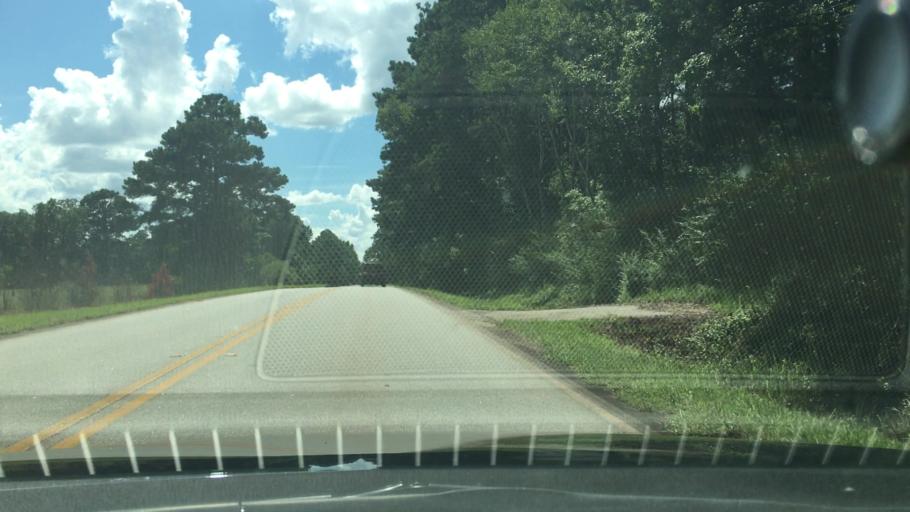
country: US
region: Georgia
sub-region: Jasper County
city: Monticello
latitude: 33.3046
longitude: -83.6170
